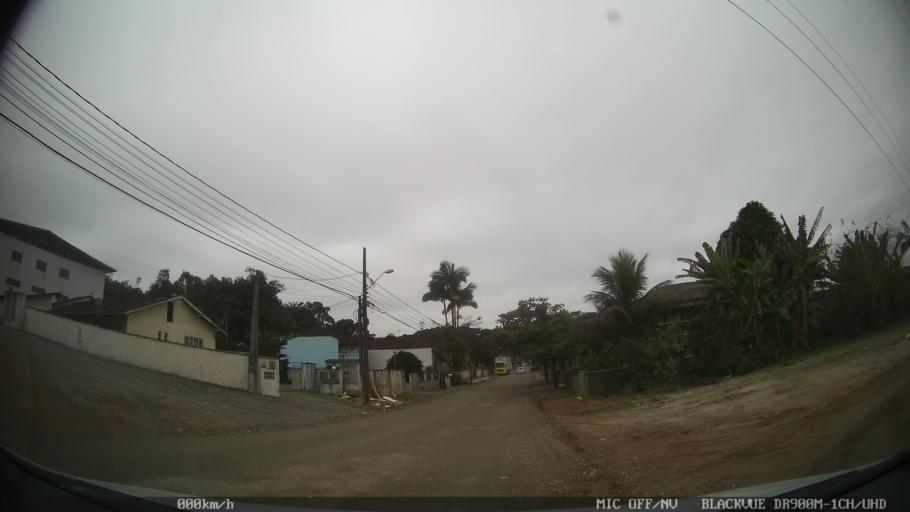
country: BR
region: Santa Catarina
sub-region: Joinville
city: Joinville
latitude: -26.2784
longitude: -48.8988
